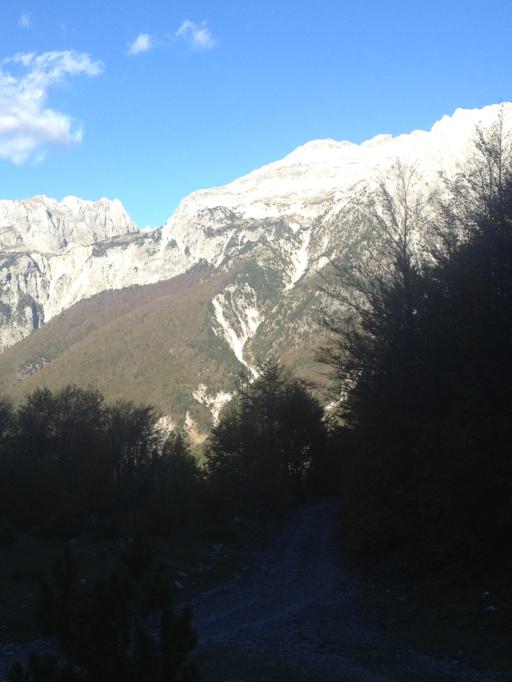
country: AL
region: Shkoder
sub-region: Rrethi i Shkodres
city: Nicaj-Shale
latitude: 42.4013
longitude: 19.7485
